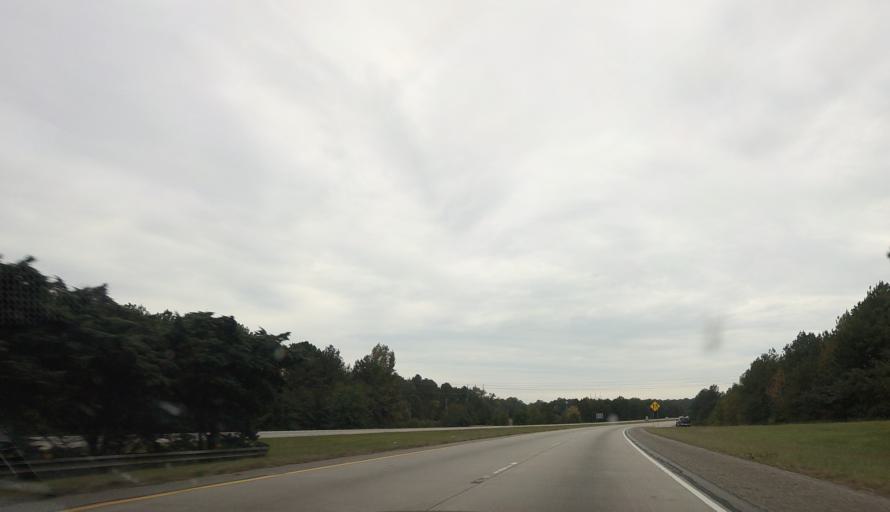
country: US
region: Alabama
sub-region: Russell County
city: Phenix City
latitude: 32.5280
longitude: -84.9764
